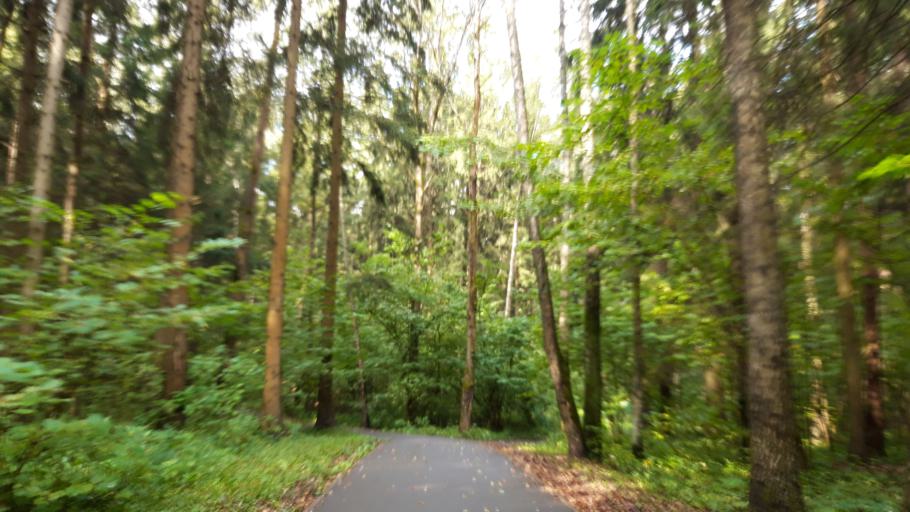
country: RU
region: Moscow
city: Zelenograd
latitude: 55.9851
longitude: 37.1992
